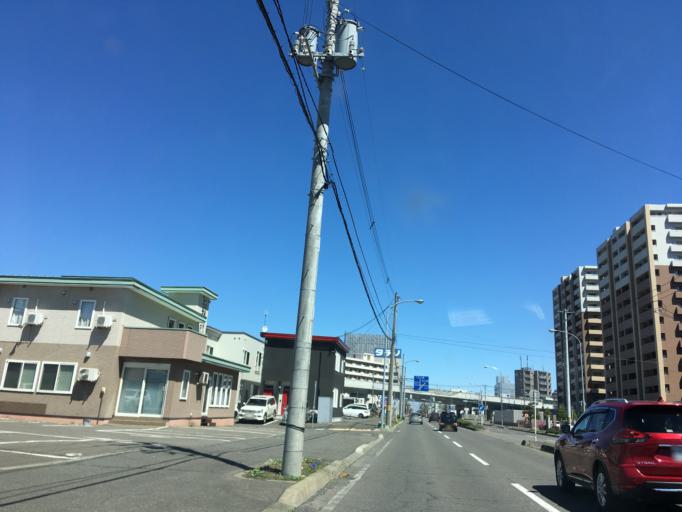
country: JP
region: Hokkaido
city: Obihiro
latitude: 42.9208
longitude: 143.1937
